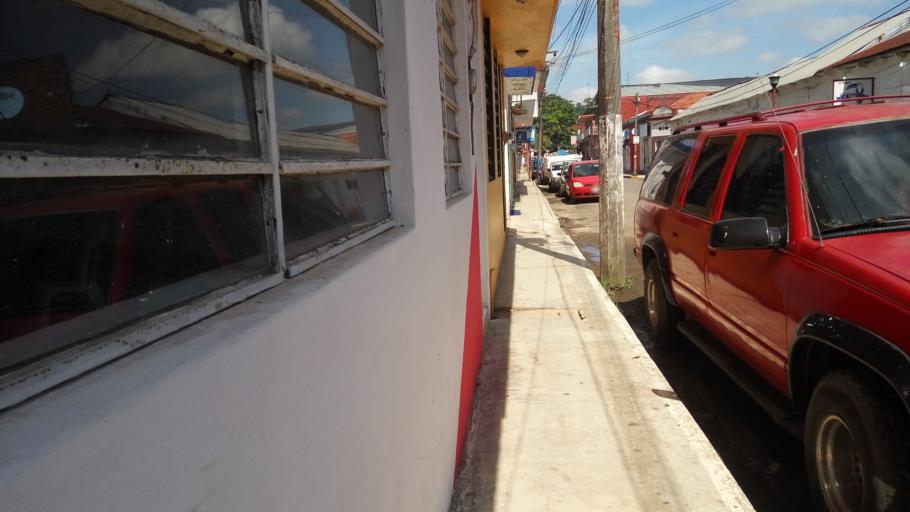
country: MX
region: Tabasco
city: Teapa
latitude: 17.5478
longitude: -92.9513
